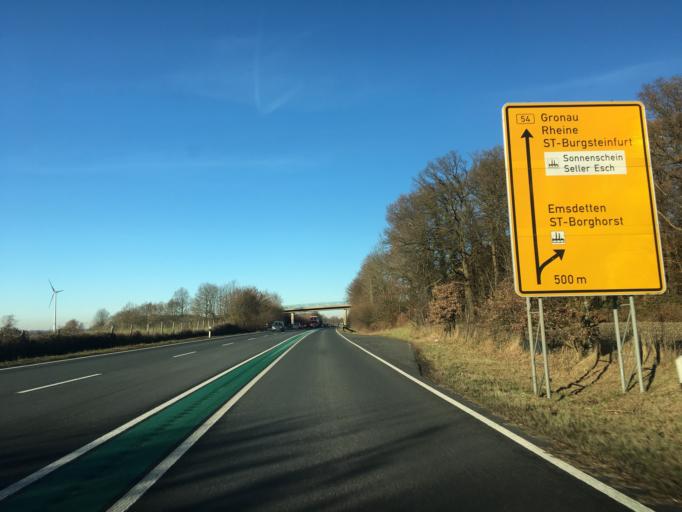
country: DE
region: North Rhine-Westphalia
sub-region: Regierungsbezirk Munster
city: Laer
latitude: 52.1065
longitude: 7.3814
